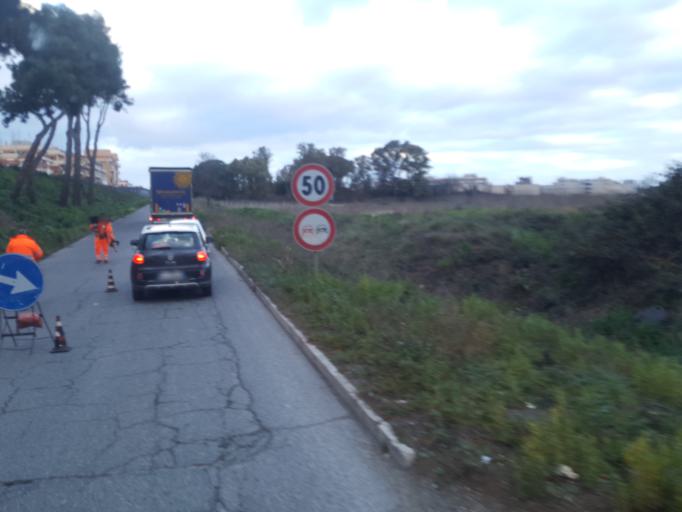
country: IT
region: Latium
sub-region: Citta metropolitana di Roma Capitale
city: Area Produttiva
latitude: 41.6737
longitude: 12.5040
